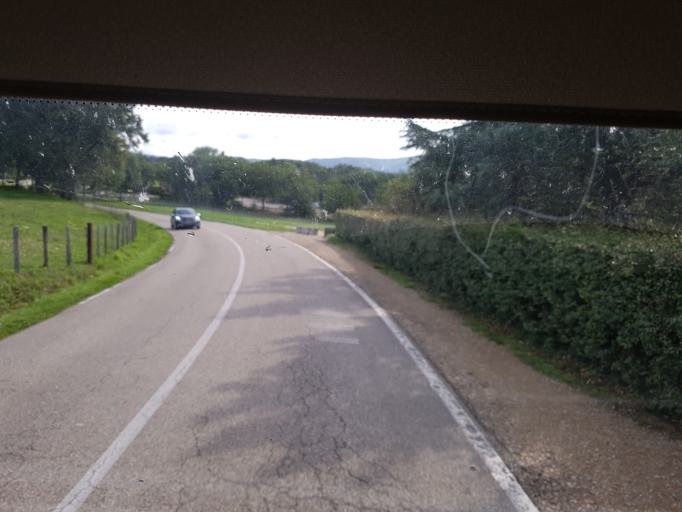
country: FR
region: Rhone-Alpes
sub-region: Departement de l'Ain
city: Bourg-en-Bresse
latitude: 46.1912
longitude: 5.2549
